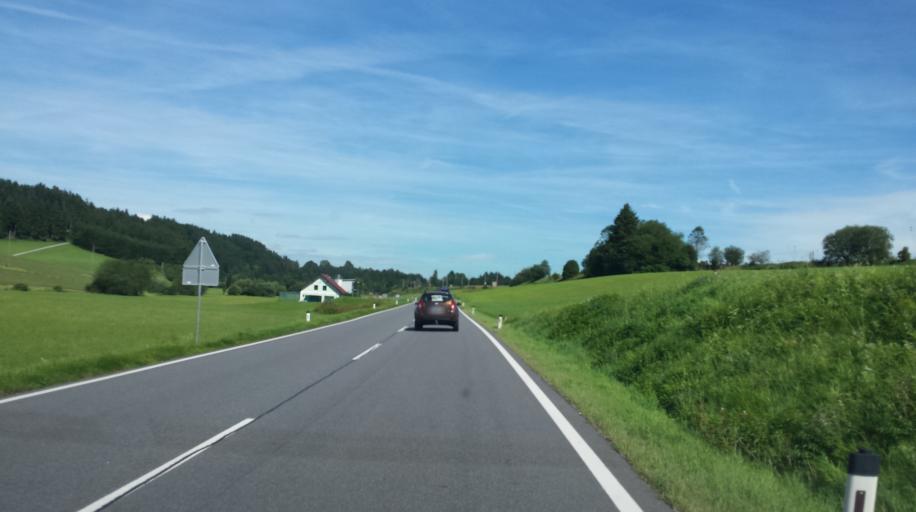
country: AT
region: Upper Austria
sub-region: Politischer Bezirk Vocklabruck
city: Frankenmarkt
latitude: 47.9865
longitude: 13.3816
